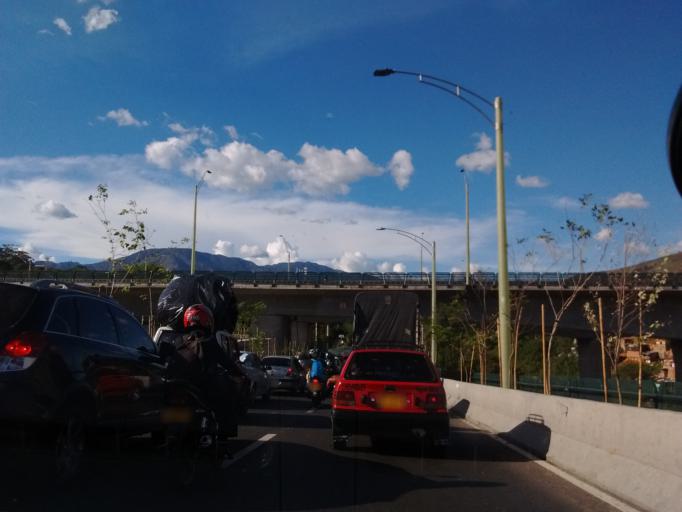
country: CO
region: Antioquia
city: Medellin
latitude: 6.2858
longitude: -75.5671
